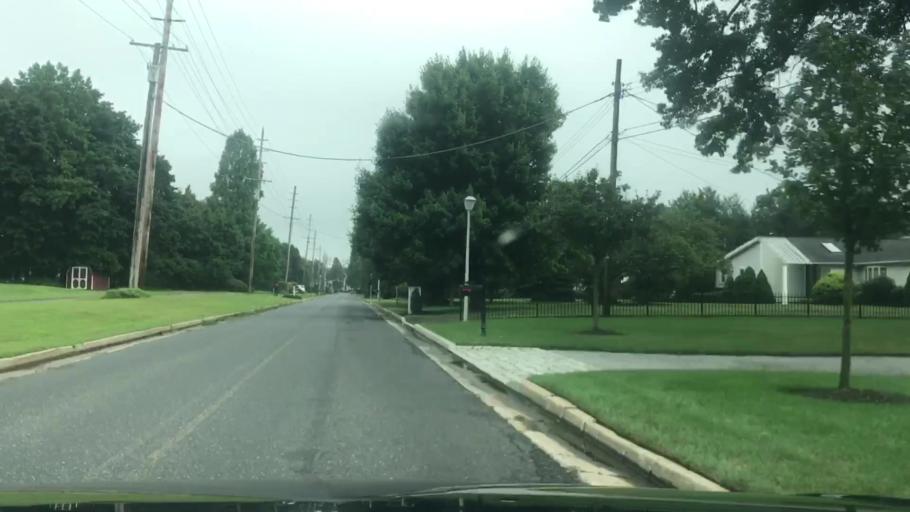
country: US
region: New Jersey
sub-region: Monmouth County
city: Little Silver
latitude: 40.3472
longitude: -74.0397
